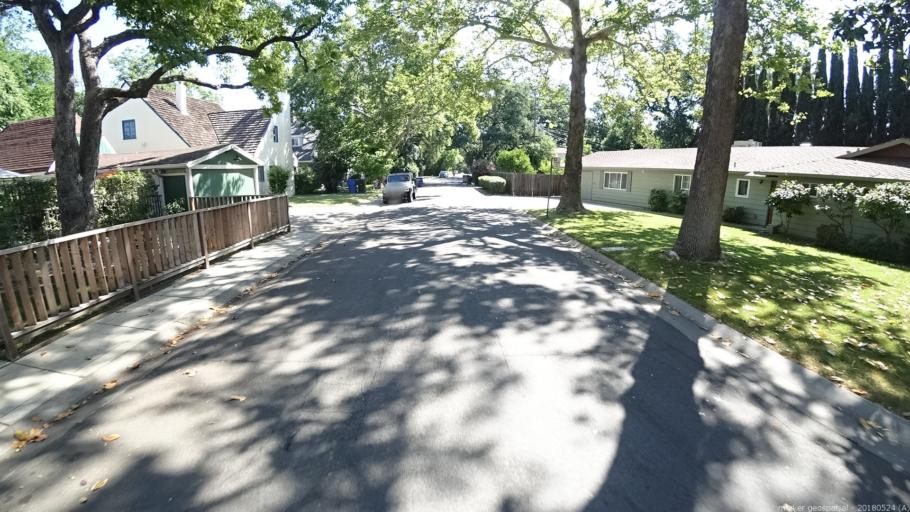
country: US
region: California
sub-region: Sacramento County
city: Sacramento
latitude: 38.6037
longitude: -121.4616
